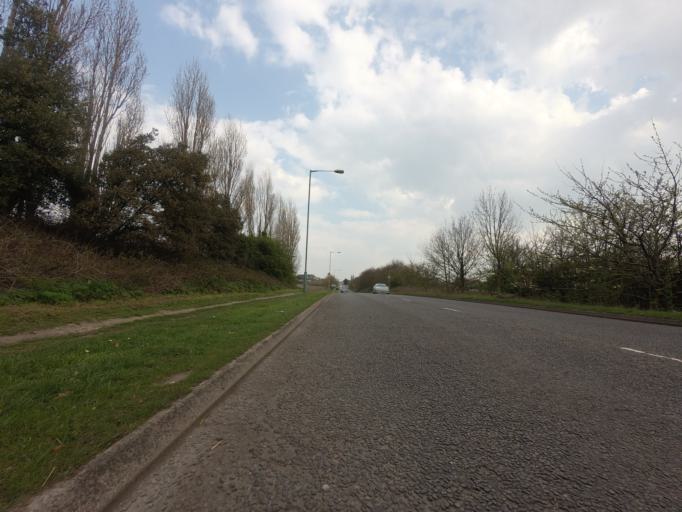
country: GB
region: England
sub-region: Kent
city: Swanley
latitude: 51.4081
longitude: 0.1507
